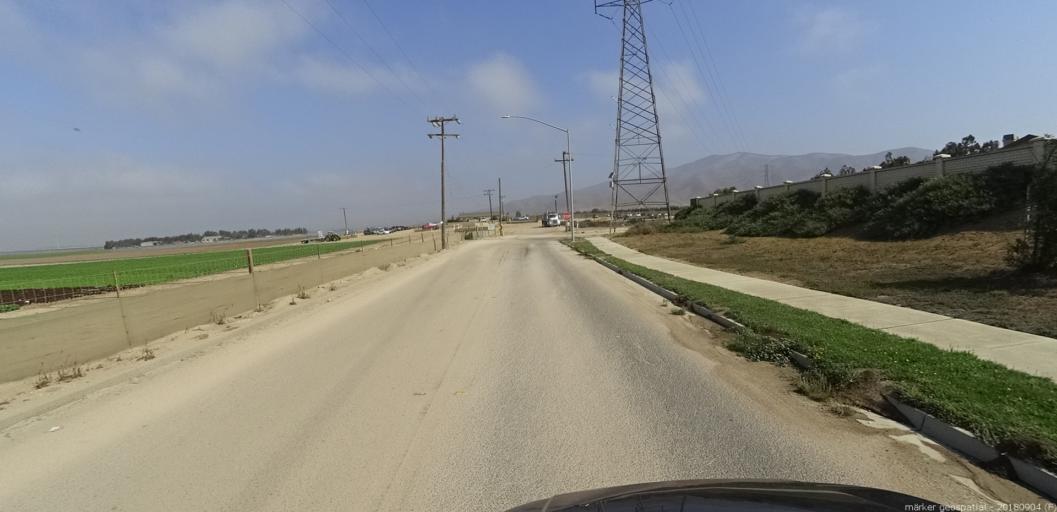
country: US
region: California
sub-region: Monterey County
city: Soledad
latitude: 36.4444
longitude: -121.3336
